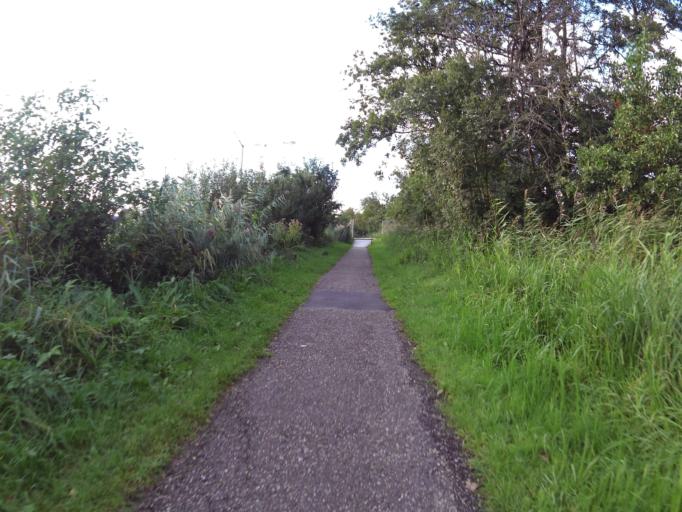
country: NL
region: South Holland
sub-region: Gemeente Nieuwkoop
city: Nieuwkoop
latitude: 52.1327
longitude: 4.7708
